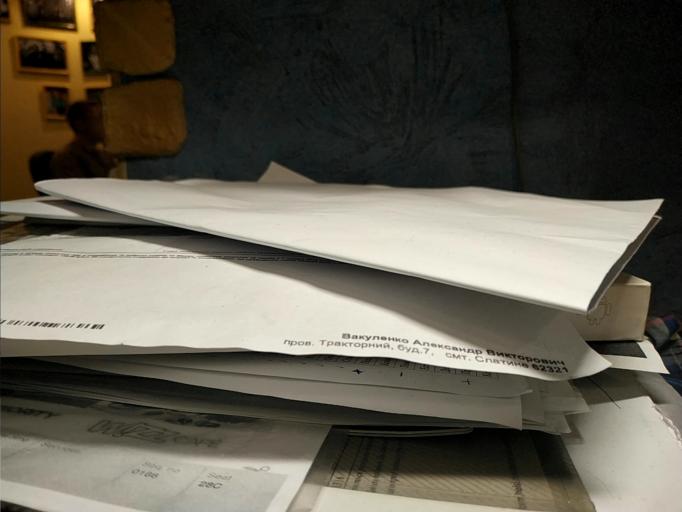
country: RU
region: Tverskaya
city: Zubtsov
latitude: 56.1226
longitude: 34.5598
